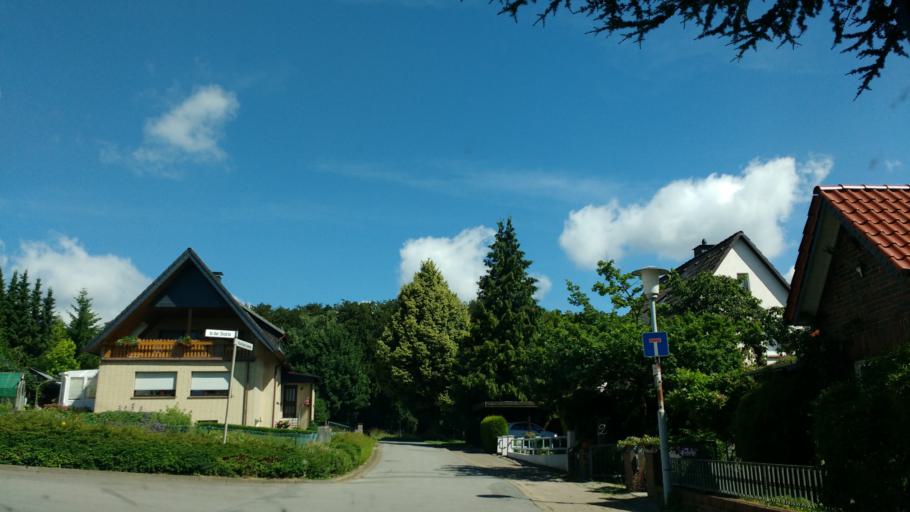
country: DE
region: North Rhine-Westphalia
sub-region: Regierungsbezirk Detmold
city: Lugde
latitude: 51.9778
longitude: 9.1952
